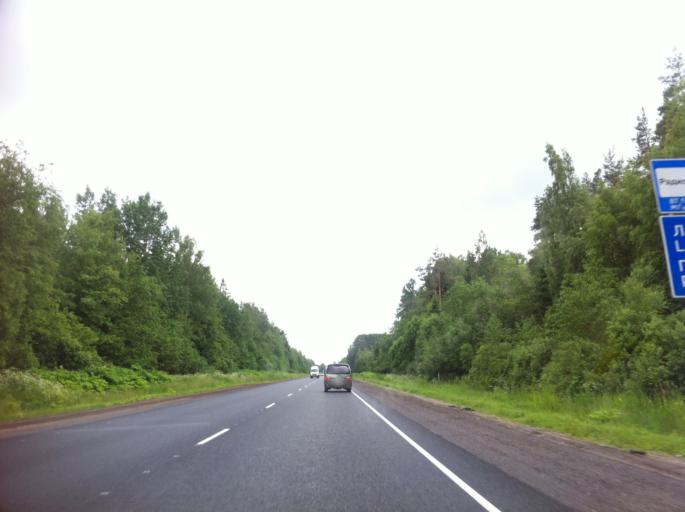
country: RU
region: Leningrad
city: Rozhdestveno
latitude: 59.1902
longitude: 29.9200
